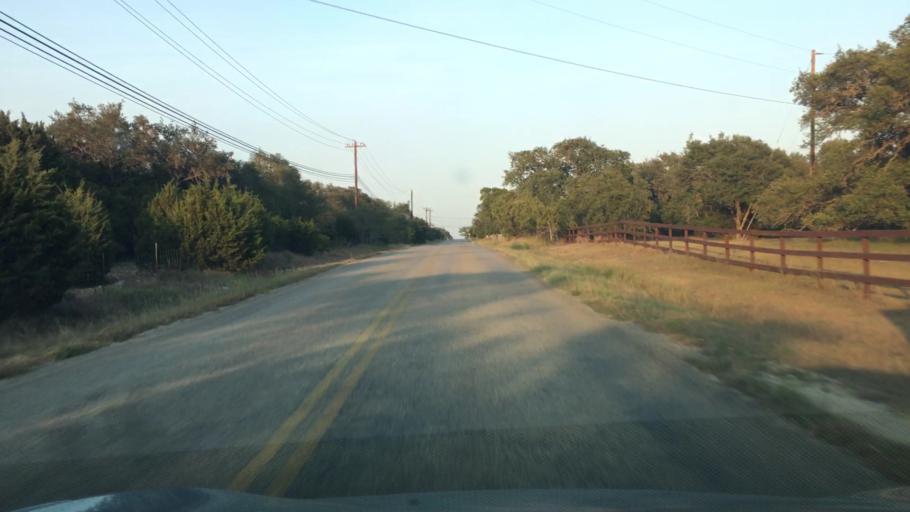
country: US
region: Texas
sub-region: Hays County
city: Dripping Springs
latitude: 30.1534
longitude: -98.0143
